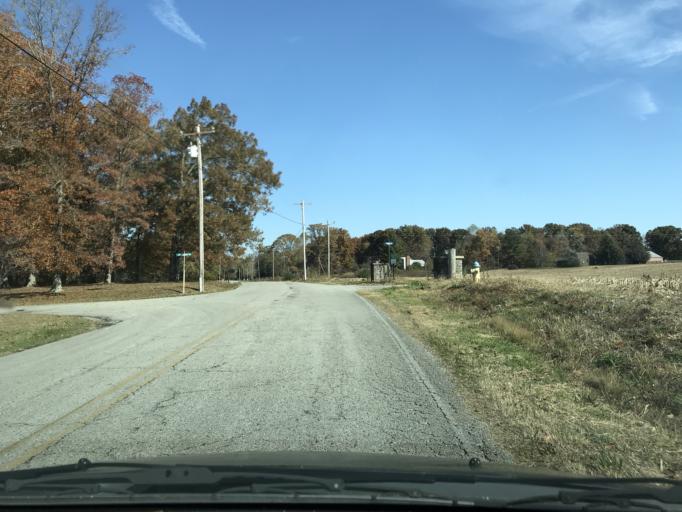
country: US
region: Tennessee
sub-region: Coffee County
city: Tullahoma
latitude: 35.4053
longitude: -86.1561
